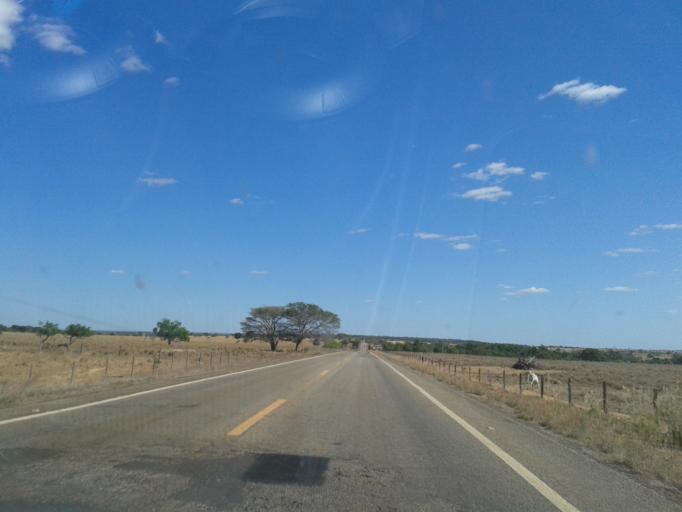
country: BR
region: Goias
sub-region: Sao Miguel Do Araguaia
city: Sao Miguel do Araguaia
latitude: -13.4329
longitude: -50.2827
